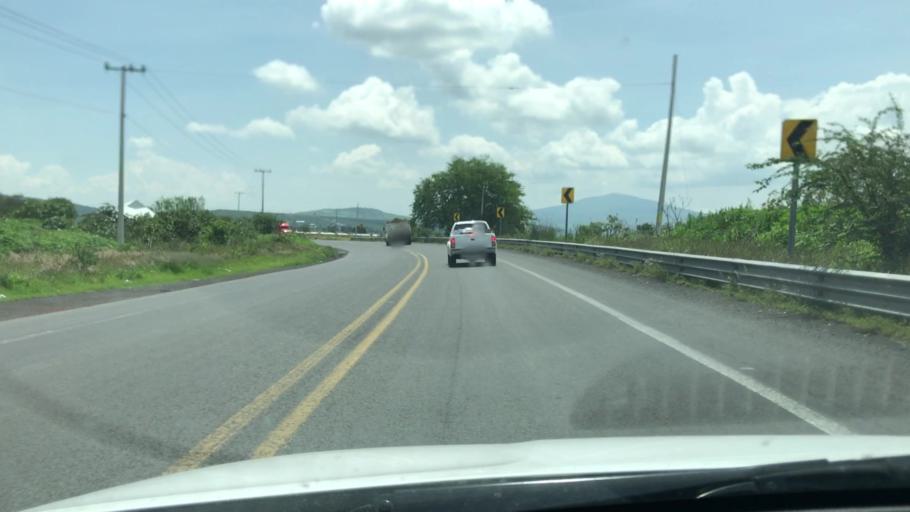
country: MX
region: Michoacan
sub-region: Yurecuaro
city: Yurecuaro
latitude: 20.3222
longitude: -102.2840
